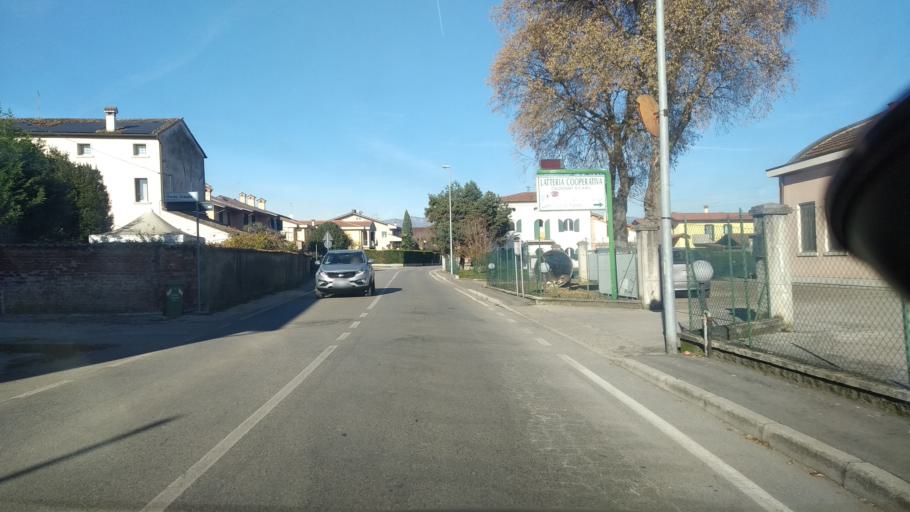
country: IT
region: Veneto
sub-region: Provincia di Vicenza
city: Caldogno-Rettorgole-Cresole
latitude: 45.6163
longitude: 11.5068
